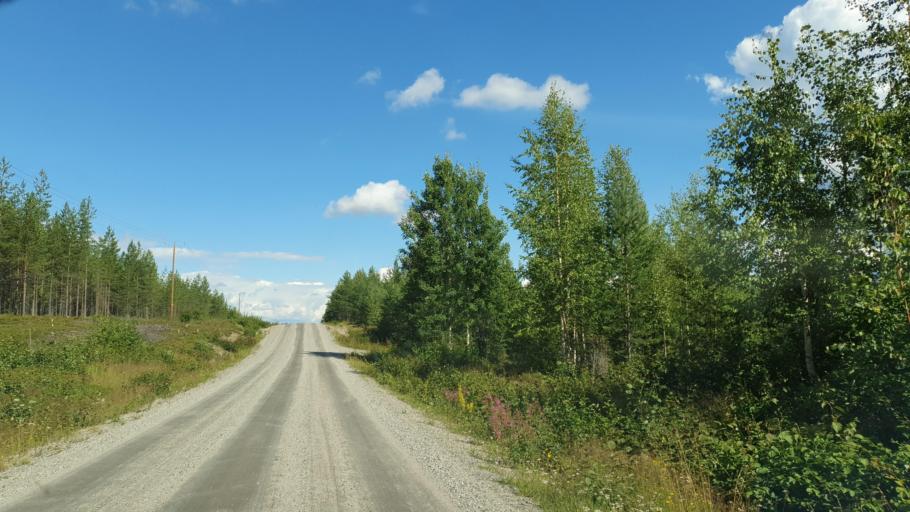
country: FI
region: Kainuu
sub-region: Kehys-Kainuu
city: Kuhmo
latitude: 64.1088
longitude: 29.3522
